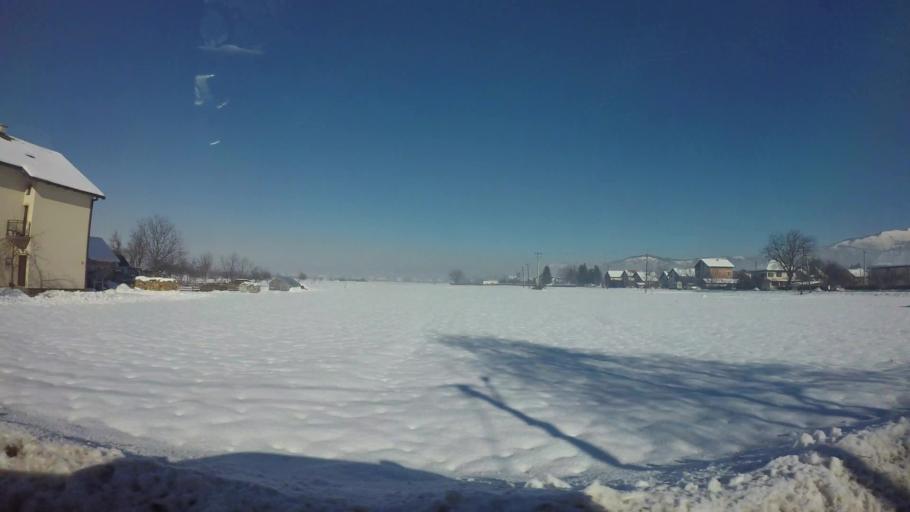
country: BA
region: Federation of Bosnia and Herzegovina
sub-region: Kanton Sarajevo
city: Sarajevo
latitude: 43.7912
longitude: 18.3373
